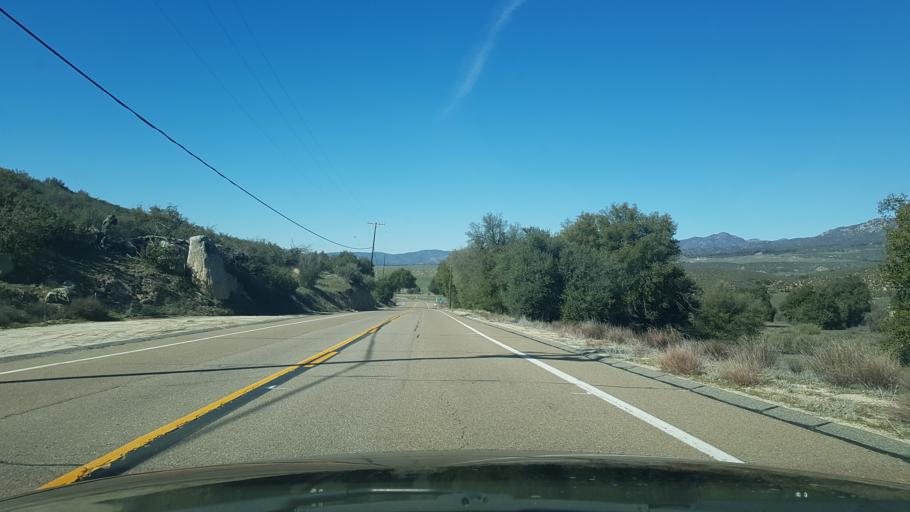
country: US
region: California
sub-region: San Diego County
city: Julian
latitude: 33.2166
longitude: -116.6026
